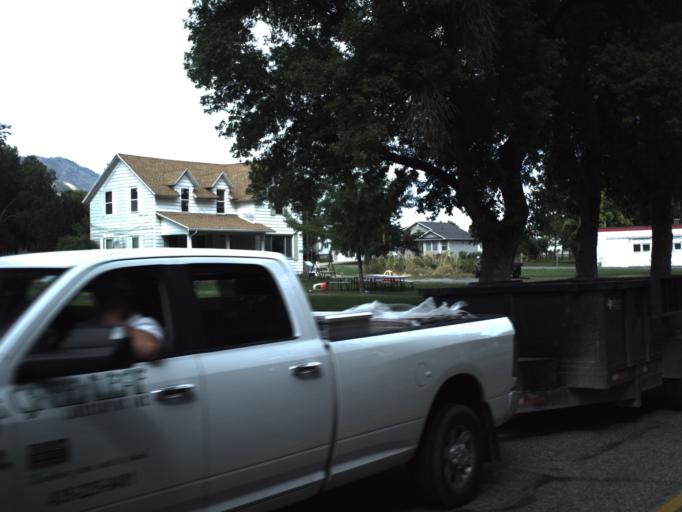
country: US
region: Utah
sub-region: Cache County
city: Wellsville
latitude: 41.6359
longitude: -111.9344
